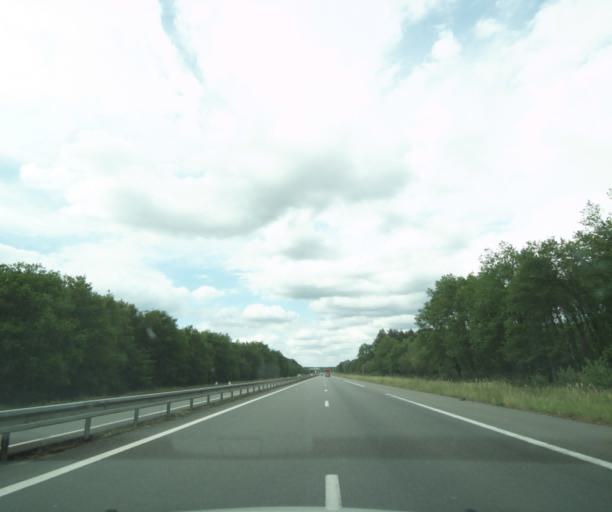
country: FR
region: Centre
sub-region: Departement du Loir-et-Cher
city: Theillay
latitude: 47.3211
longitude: 2.0498
